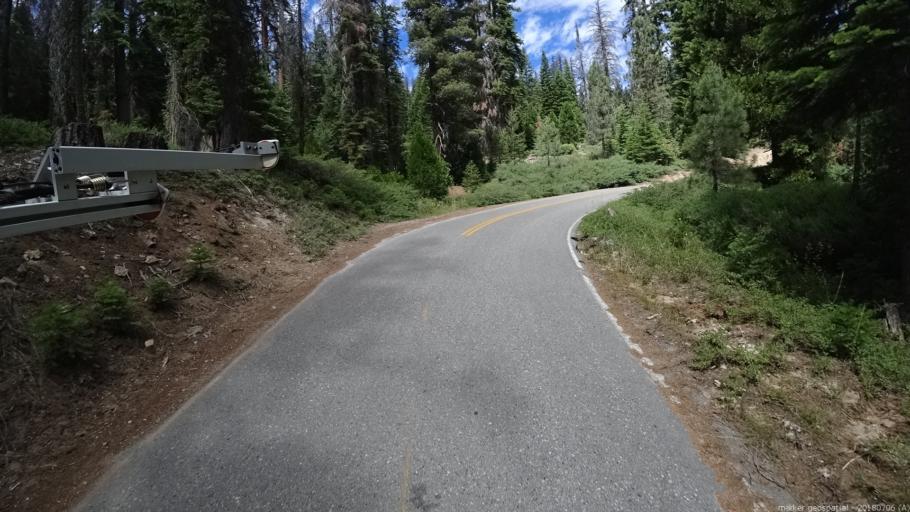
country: US
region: California
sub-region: Madera County
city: Oakhurst
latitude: 37.4295
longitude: -119.4150
